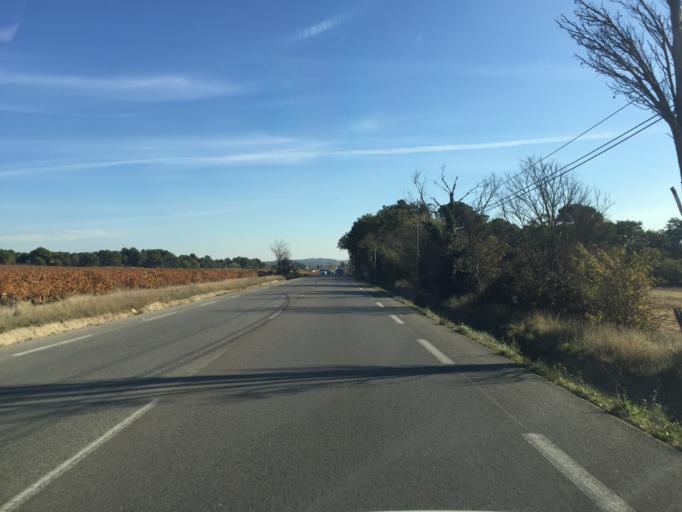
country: FR
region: Provence-Alpes-Cote d'Azur
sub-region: Departement des Bouches-du-Rhone
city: Eguilles
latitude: 43.5918
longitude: 5.3600
